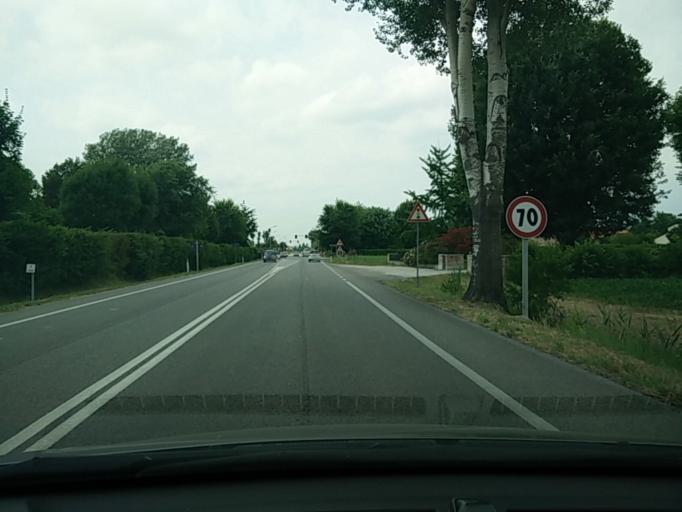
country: IT
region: Veneto
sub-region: Provincia di Venezia
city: Summaga
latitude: 45.7806
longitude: 12.8011
